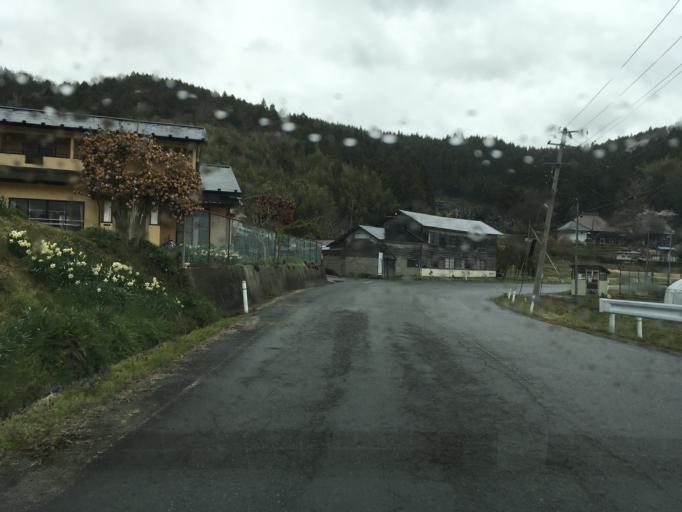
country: JP
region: Iwate
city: Ichinoseki
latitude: 38.7528
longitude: 141.2257
